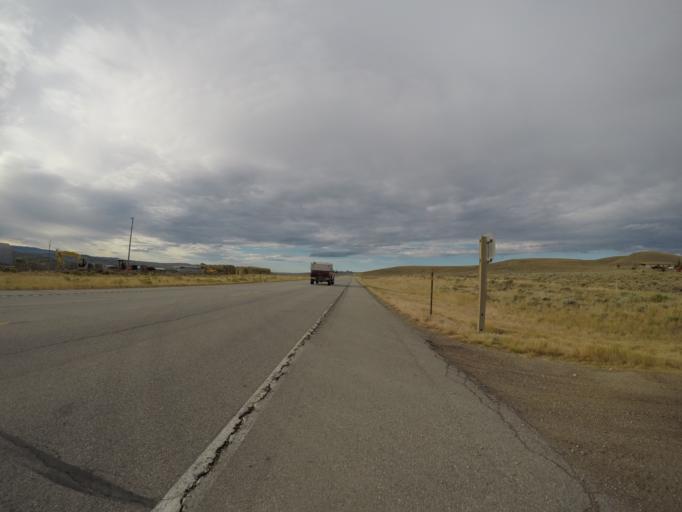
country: US
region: Wyoming
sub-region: Carbon County
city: Saratoga
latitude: 41.3725
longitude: -106.7468
